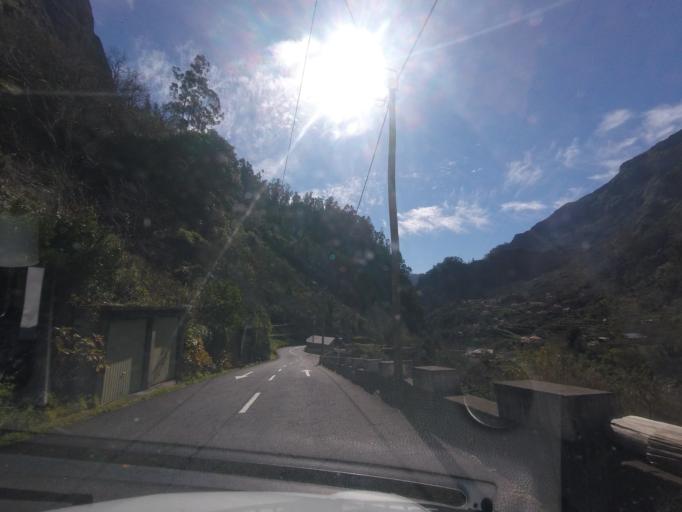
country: PT
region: Madeira
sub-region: Camara de Lobos
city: Curral das Freiras
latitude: 32.7384
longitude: -16.9682
